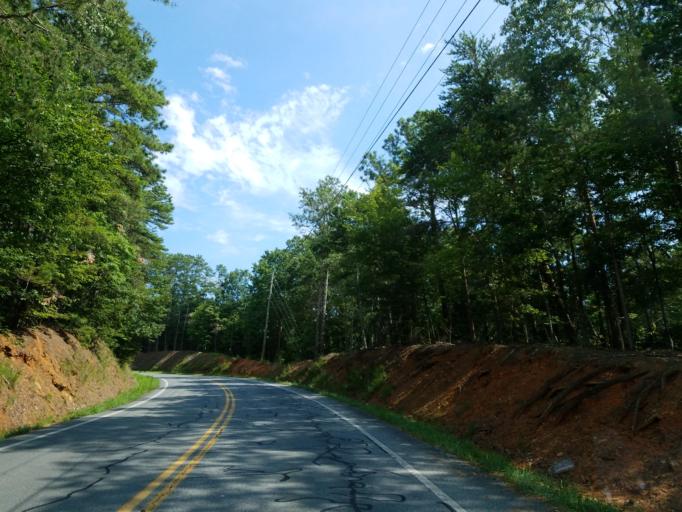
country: US
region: Georgia
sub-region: Gilmer County
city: Ellijay
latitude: 34.5831
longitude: -84.6099
